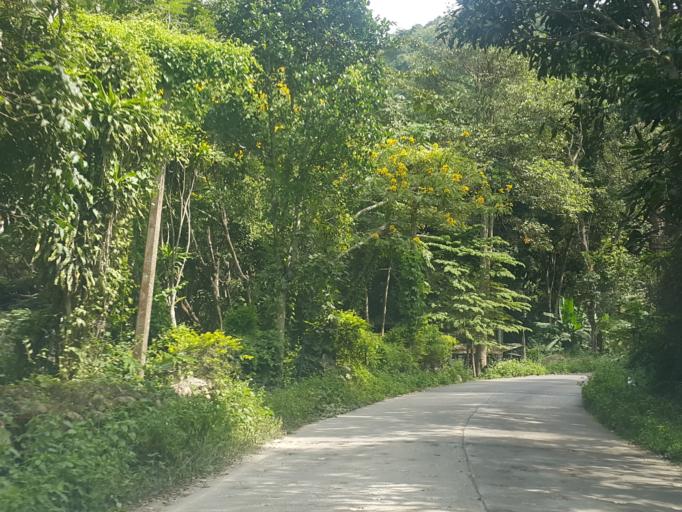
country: TH
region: Chiang Mai
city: Mae On
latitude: 18.8695
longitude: 99.3177
